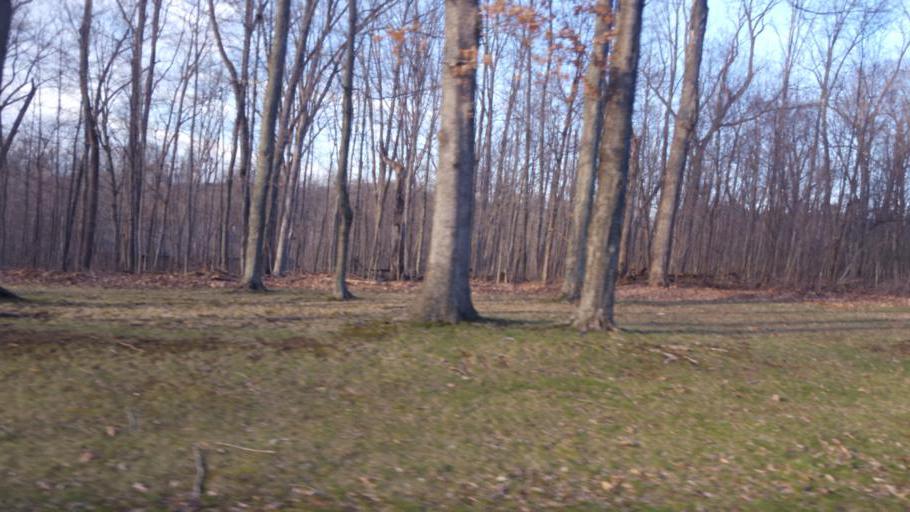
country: US
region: Ohio
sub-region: Knox County
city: Gambier
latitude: 40.4291
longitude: -82.3418
